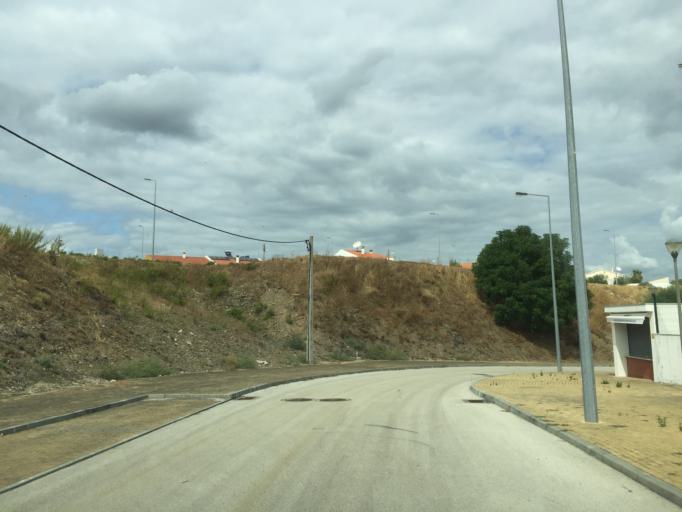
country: PT
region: Portalegre
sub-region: Ponte de Sor
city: Santo Andre
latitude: 39.0813
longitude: -8.1746
